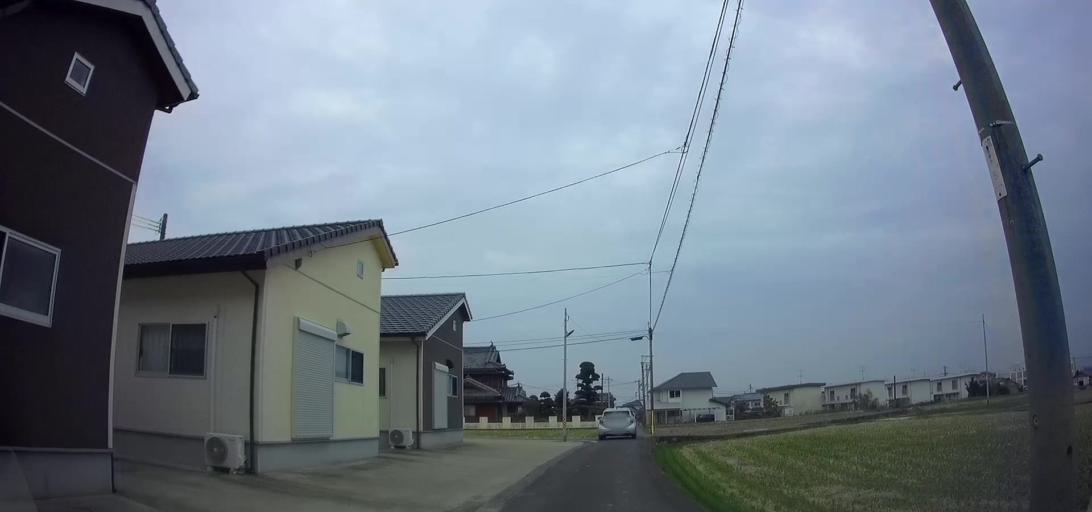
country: JP
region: Nagasaki
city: Shimabara
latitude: 32.6639
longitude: 130.2989
